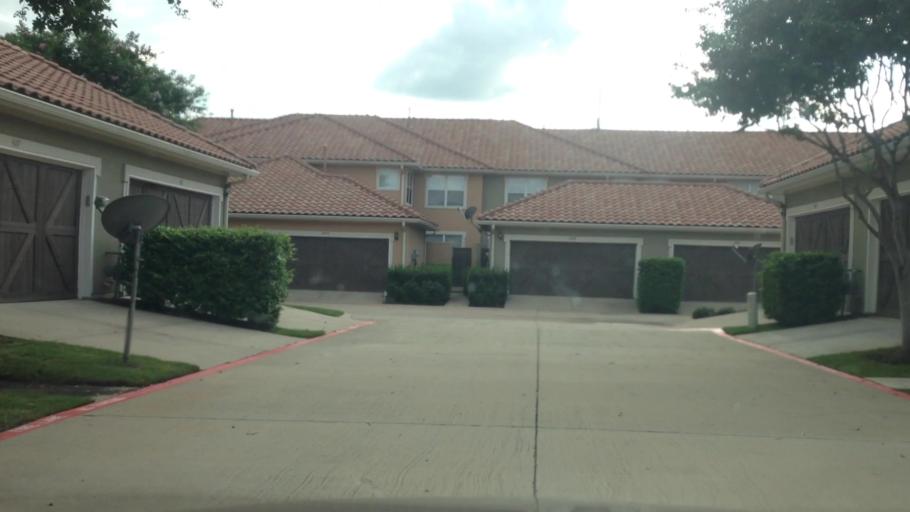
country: US
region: Texas
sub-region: Dallas County
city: Farmers Branch
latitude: 32.9031
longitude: -96.9391
